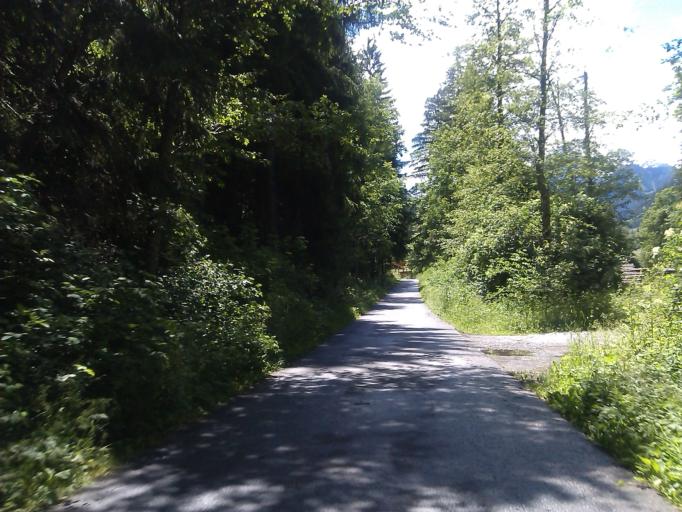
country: AT
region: Tyrol
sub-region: Politischer Bezirk Landeck
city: Pfunds
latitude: 46.9850
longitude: 10.5712
